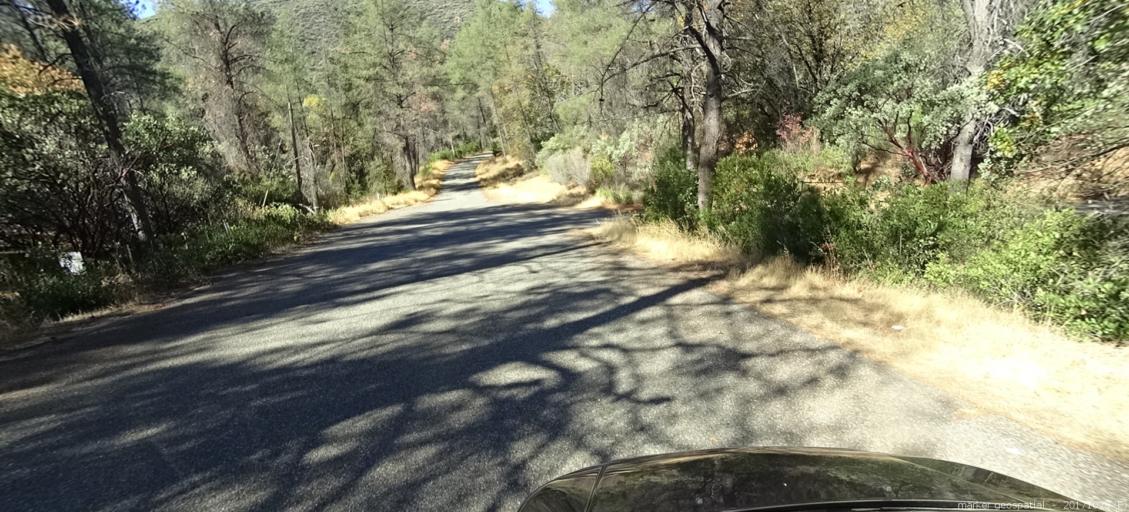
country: US
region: California
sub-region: Shasta County
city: Shasta
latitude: 40.6528
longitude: -122.5977
